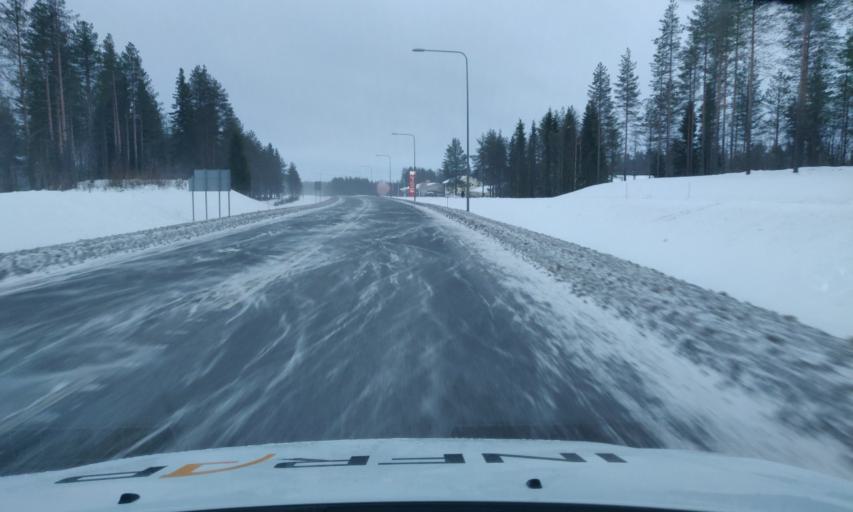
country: FI
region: Northern Ostrobothnia
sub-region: Koillismaa
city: Kuusamo
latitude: 65.9918
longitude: 29.1536
